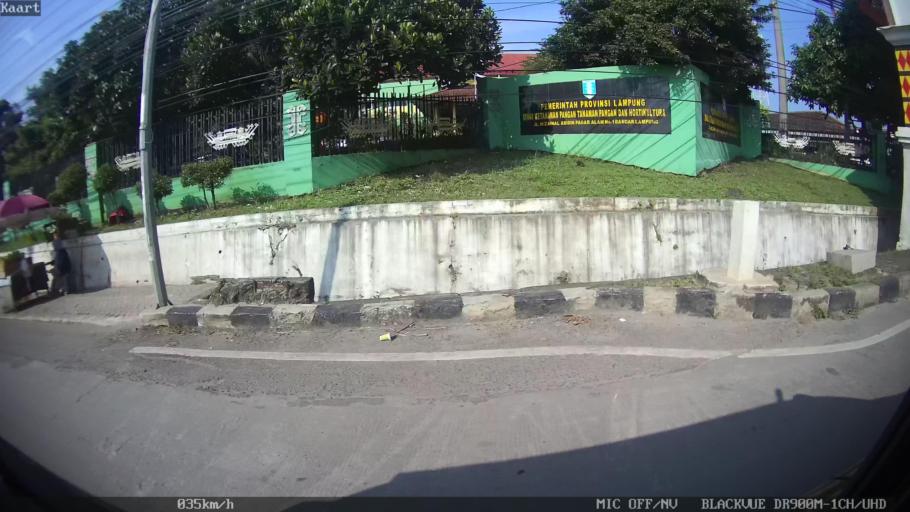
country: ID
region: Lampung
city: Kedaton
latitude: -5.3629
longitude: 105.2263
